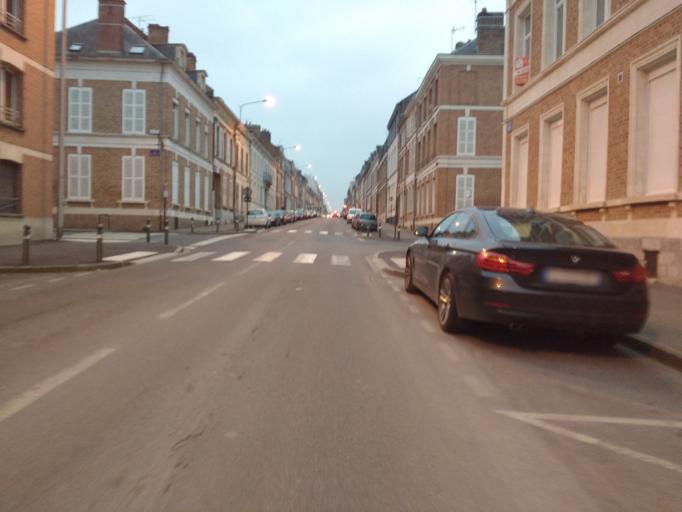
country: FR
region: Picardie
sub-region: Departement de la Somme
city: Amiens
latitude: 49.8871
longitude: 2.2968
